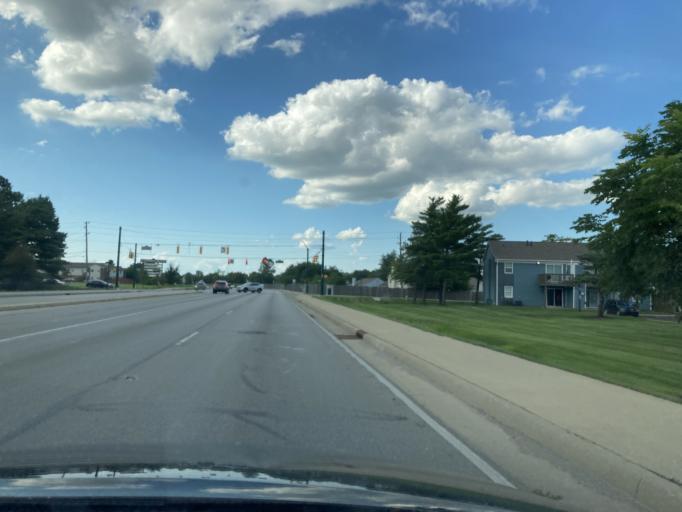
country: US
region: Indiana
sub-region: Marion County
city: Speedway
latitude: 39.8597
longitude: -86.2409
